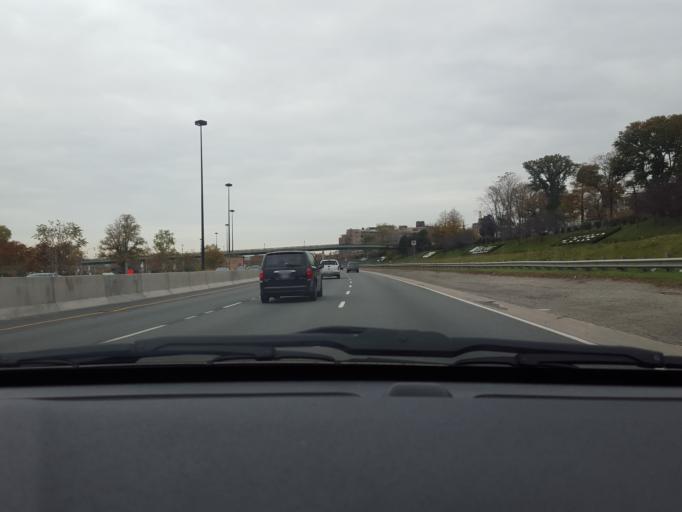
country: CA
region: Ontario
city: Toronto
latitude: 43.6367
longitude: -79.4433
